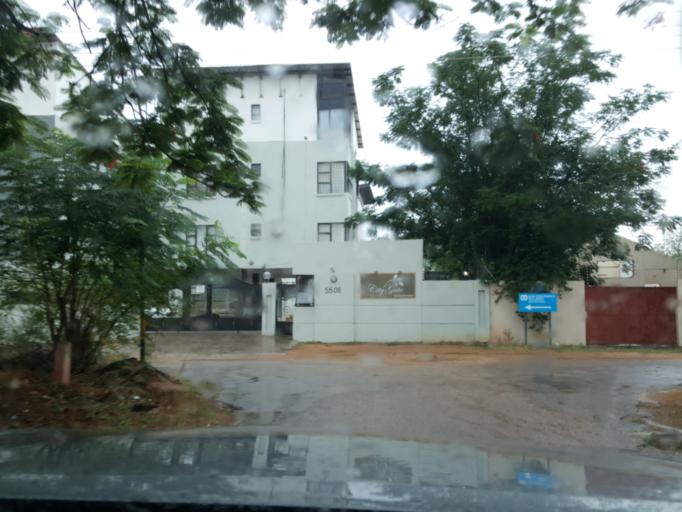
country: BW
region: South East
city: Gaborone
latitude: -24.6421
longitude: 25.9227
